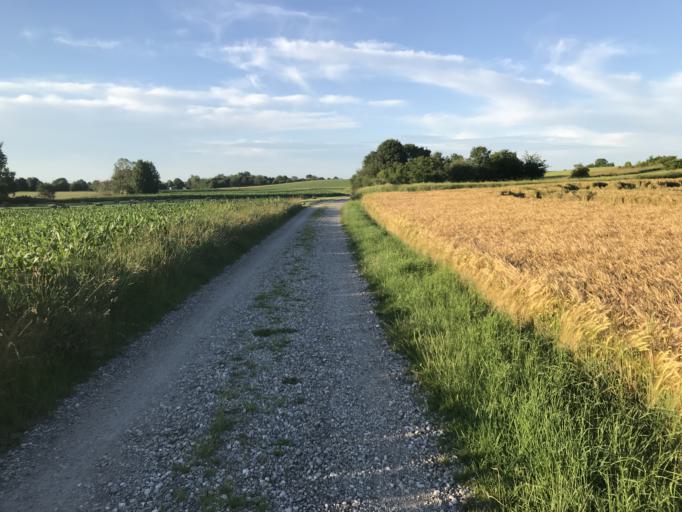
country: DE
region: Bavaria
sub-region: Swabia
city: Merching
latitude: 48.2519
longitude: 10.9645
